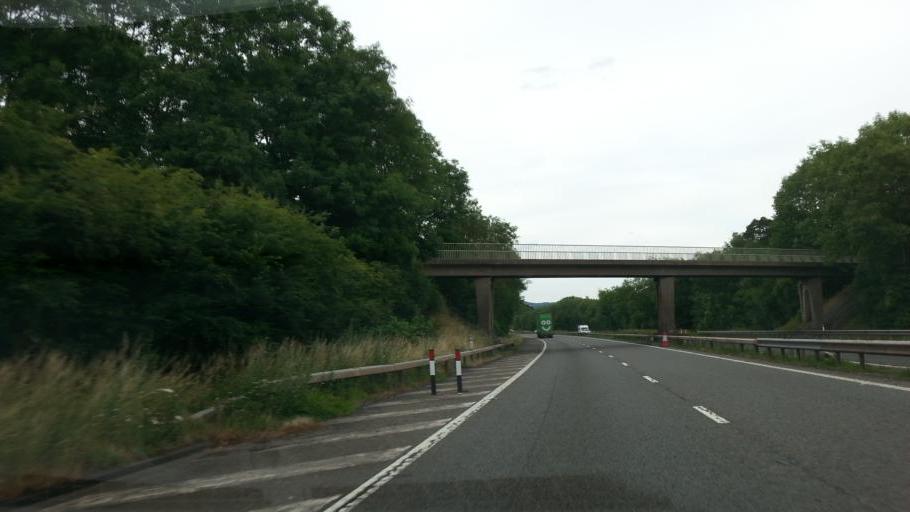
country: GB
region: England
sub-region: Herefordshire
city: Donnington
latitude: 51.9747
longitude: -2.4156
